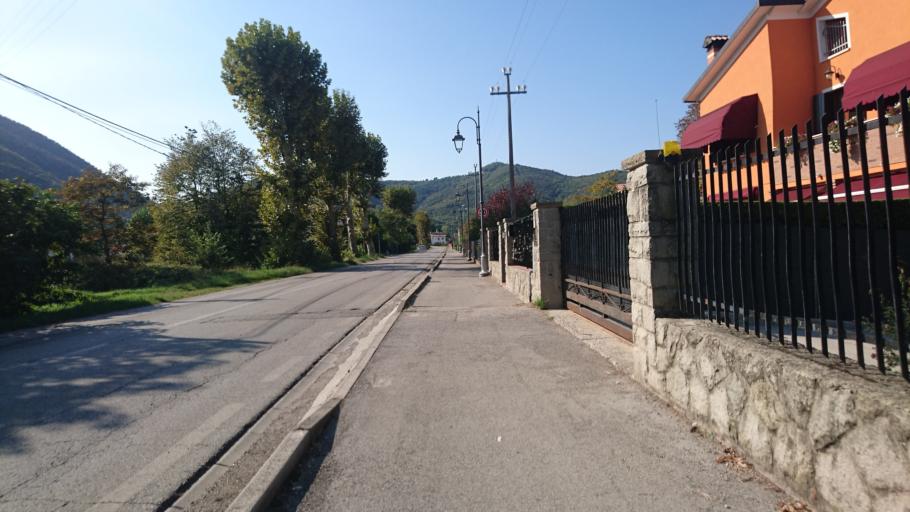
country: IT
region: Veneto
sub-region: Provincia di Padova
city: Galzignano
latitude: 45.2889
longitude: 11.7407
